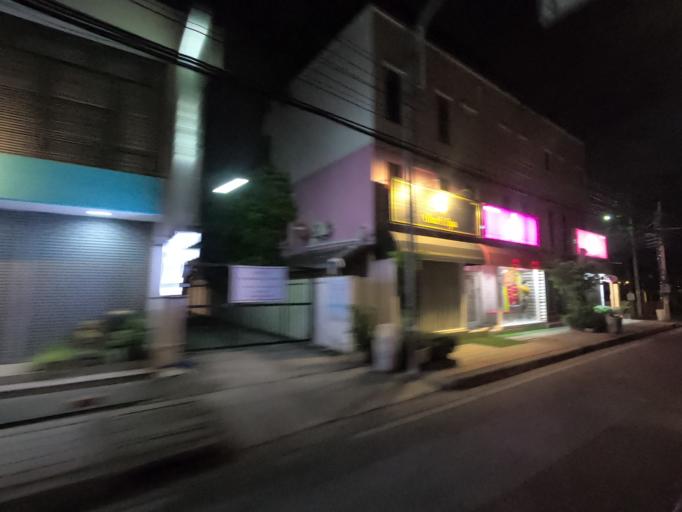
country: TH
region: Bangkok
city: Lat Phrao
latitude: 13.7985
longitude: 100.6068
